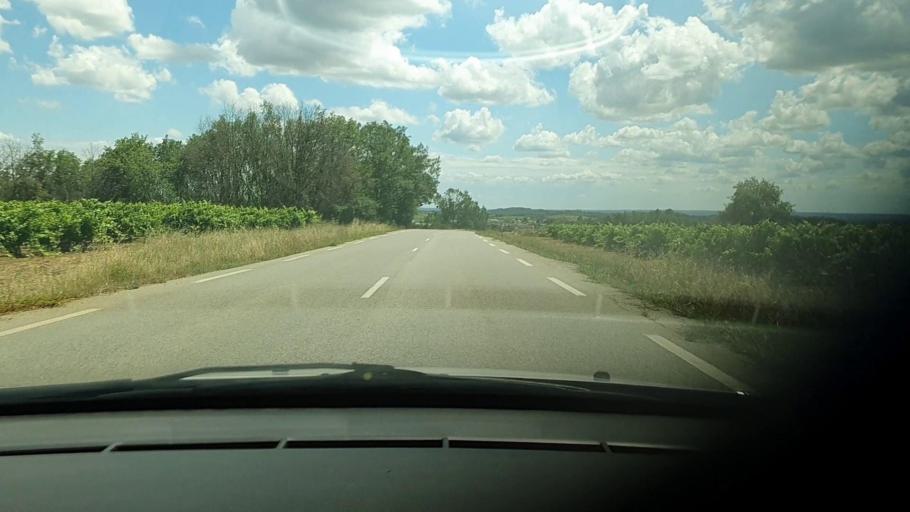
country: FR
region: Languedoc-Roussillon
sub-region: Departement du Gard
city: Moussac
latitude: 44.0454
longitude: 4.2323
